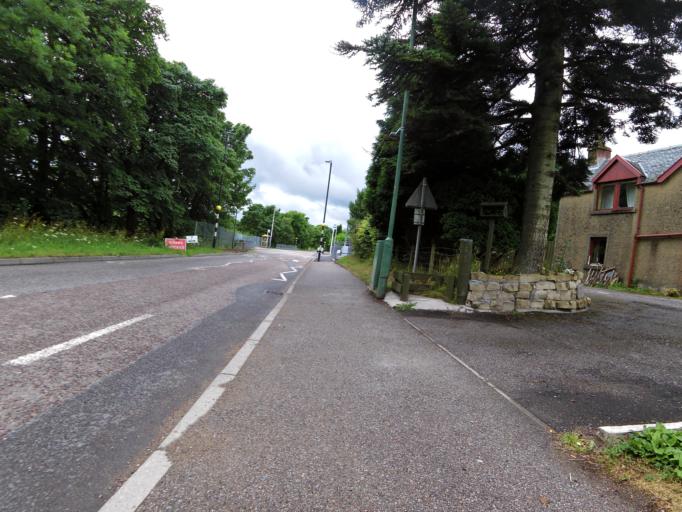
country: GB
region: Scotland
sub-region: Highland
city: Fort William
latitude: 56.8341
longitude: -5.0867
